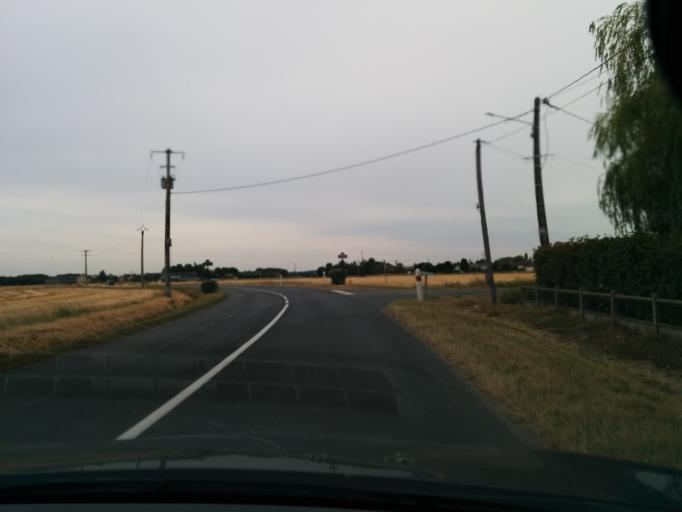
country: FR
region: Centre
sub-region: Departement du Loiret
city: Chateauneuf-sur-Loire
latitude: 47.8311
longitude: 2.2213
